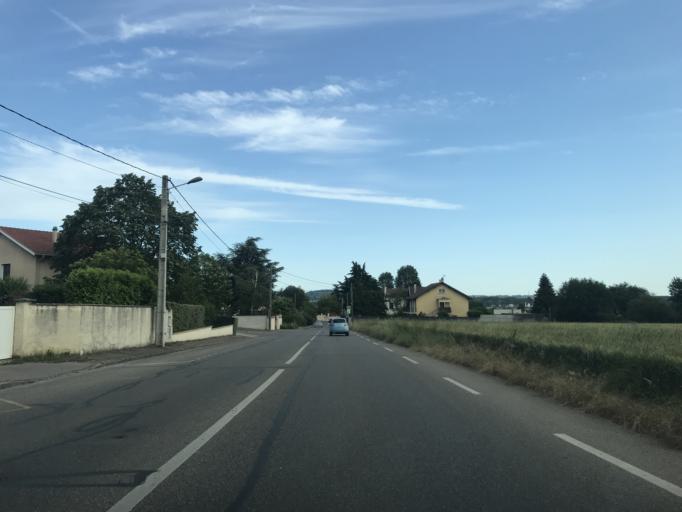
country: FR
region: Rhone-Alpes
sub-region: Departement du Rhone
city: Toussieu
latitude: 45.6915
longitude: 4.9830
